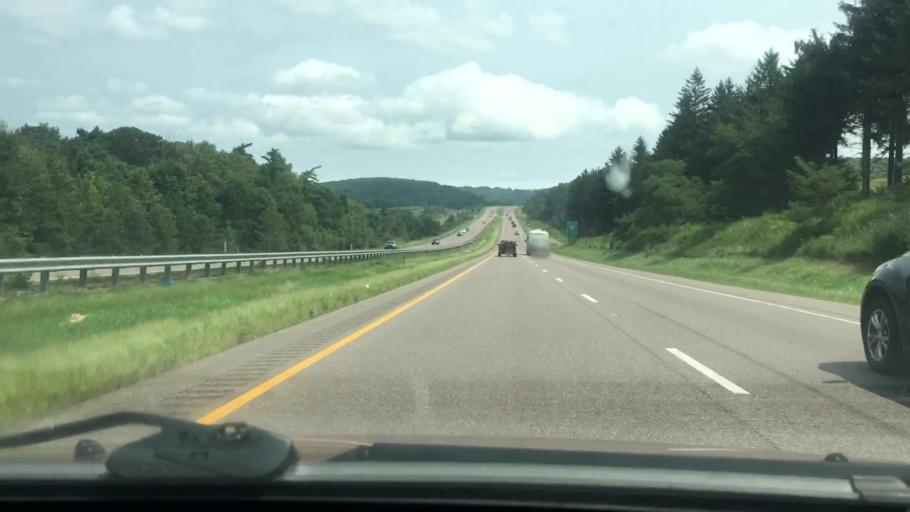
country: US
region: Maryland
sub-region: Allegany County
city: Frostburg
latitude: 39.6846
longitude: -78.9929
